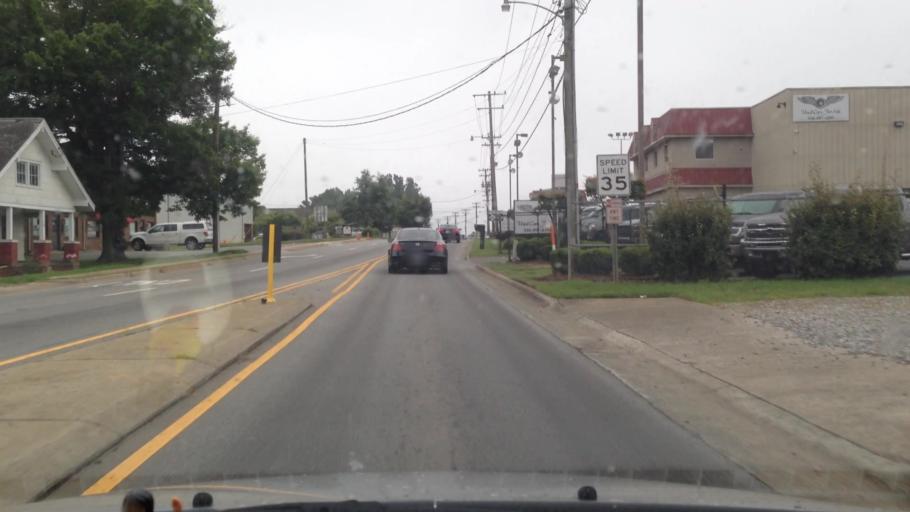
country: US
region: North Carolina
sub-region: Forsyth County
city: Kernersville
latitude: 36.1224
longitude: -80.0706
